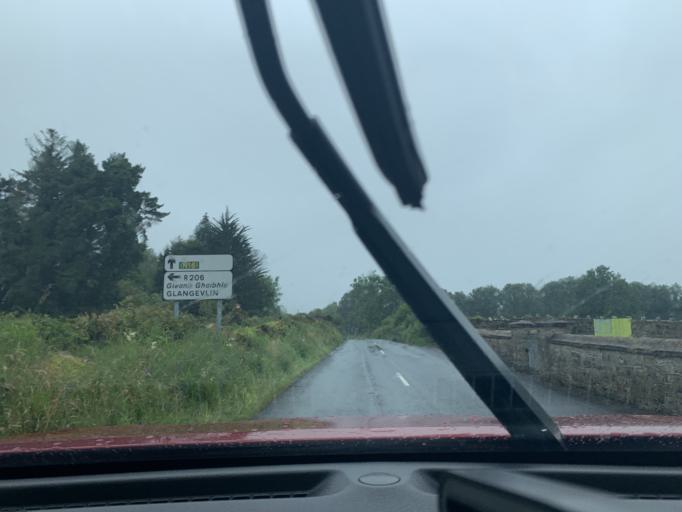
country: IE
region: Connaught
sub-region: County Leitrim
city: Manorhamilton
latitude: 54.2868
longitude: -7.9069
